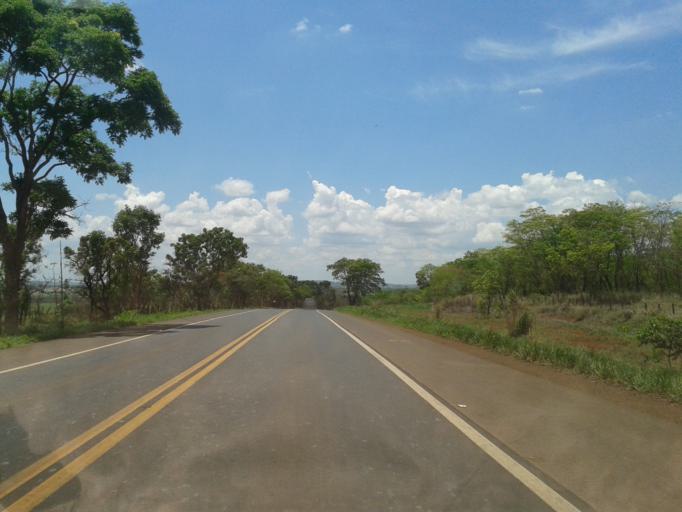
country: BR
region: Goias
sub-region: Goiatuba
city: Goiatuba
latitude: -18.2892
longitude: -49.6039
